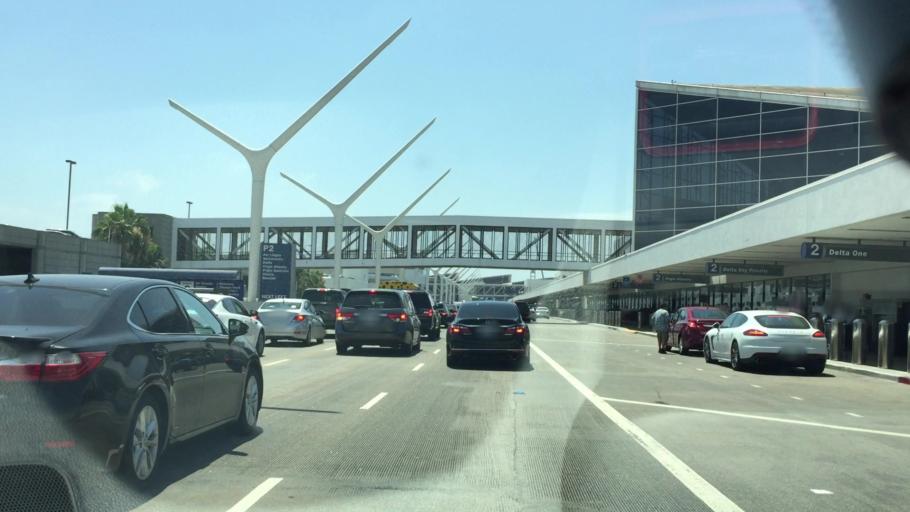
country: US
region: California
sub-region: Los Angeles County
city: El Segundo
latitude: 33.9453
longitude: -118.4031
